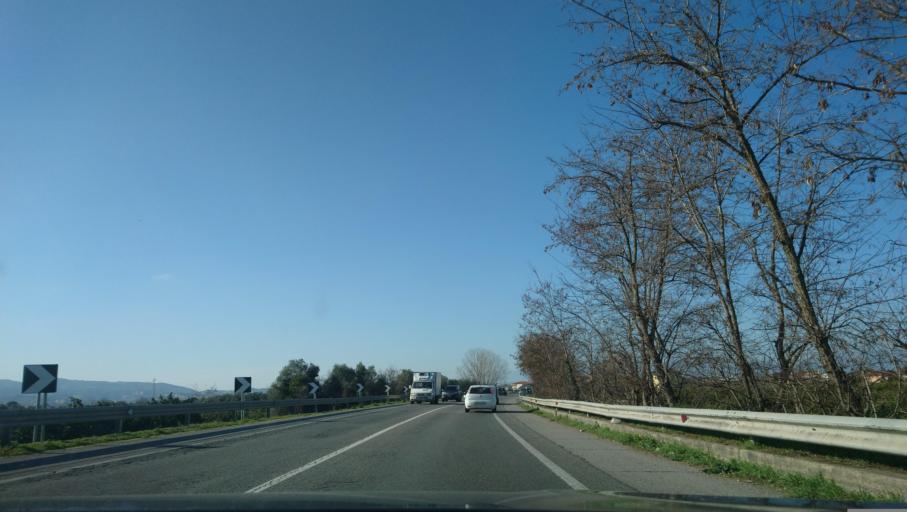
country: IT
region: Calabria
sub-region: Provincia di Cosenza
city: Fabrizio
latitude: 39.6329
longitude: 16.5557
